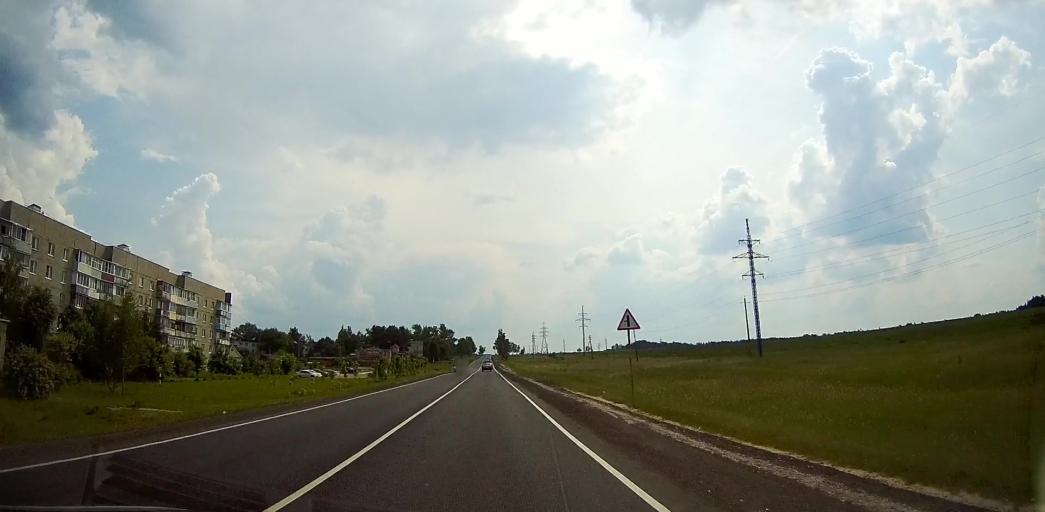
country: RU
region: Moskovskaya
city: Stupino
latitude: 54.9427
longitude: 38.1340
